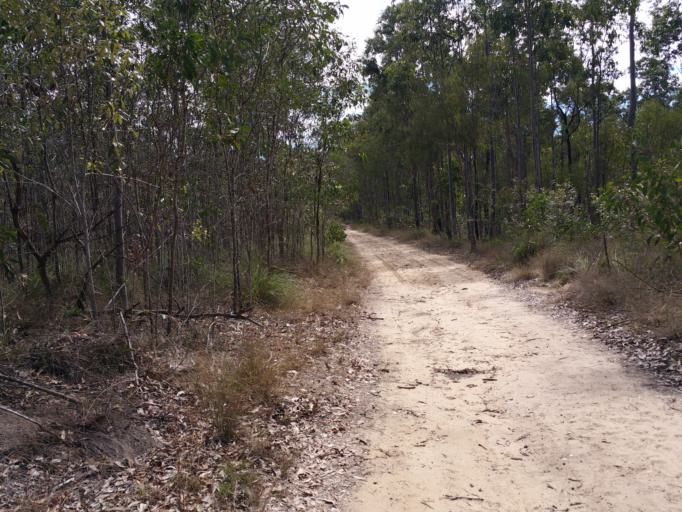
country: AU
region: Queensland
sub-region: Ipswich
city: Springfield Lakes
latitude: -27.6839
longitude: 152.9268
